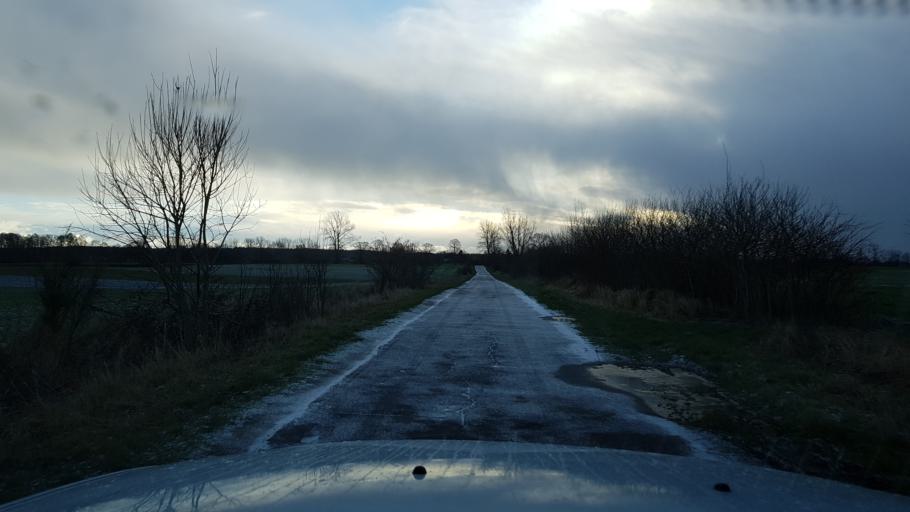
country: PL
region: West Pomeranian Voivodeship
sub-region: Powiat gryficki
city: Brojce
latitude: 54.0398
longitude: 15.3524
